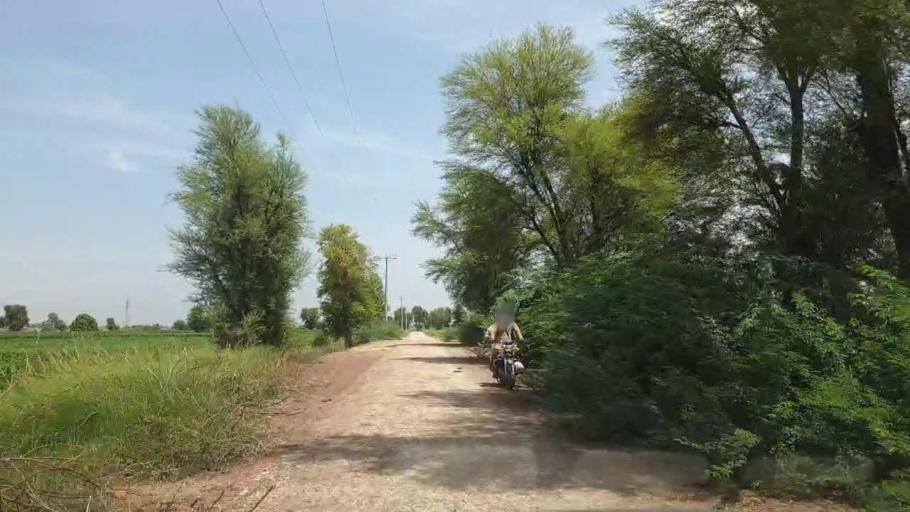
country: PK
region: Sindh
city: Kot Diji
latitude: 27.1492
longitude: 69.0168
